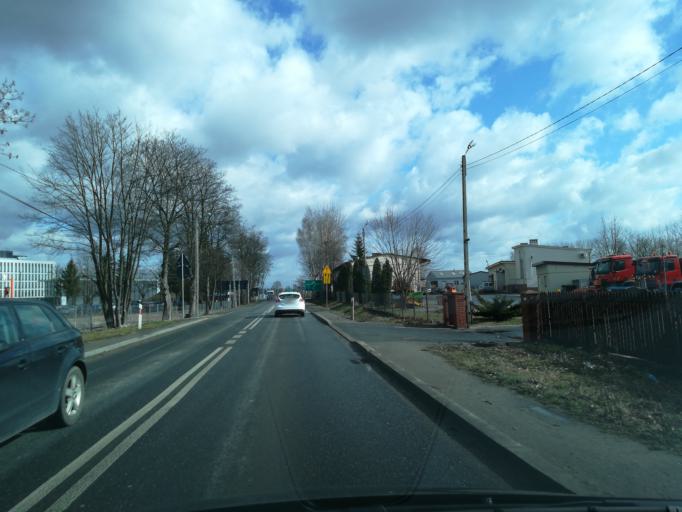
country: PL
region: Lesser Poland Voivodeship
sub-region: Powiat krakowski
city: Balice
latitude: 50.0694
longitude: 19.8020
